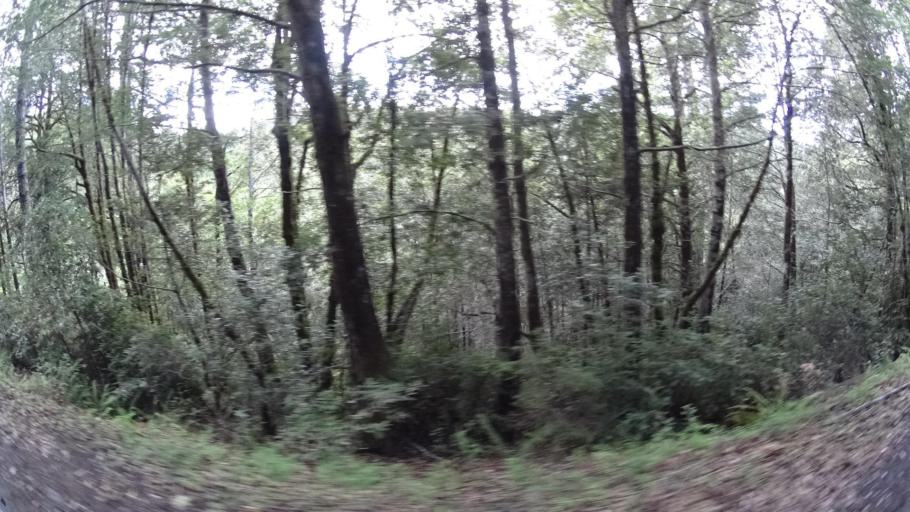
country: US
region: California
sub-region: Humboldt County
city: Blue Lake
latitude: 40.7579
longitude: -123.9704
